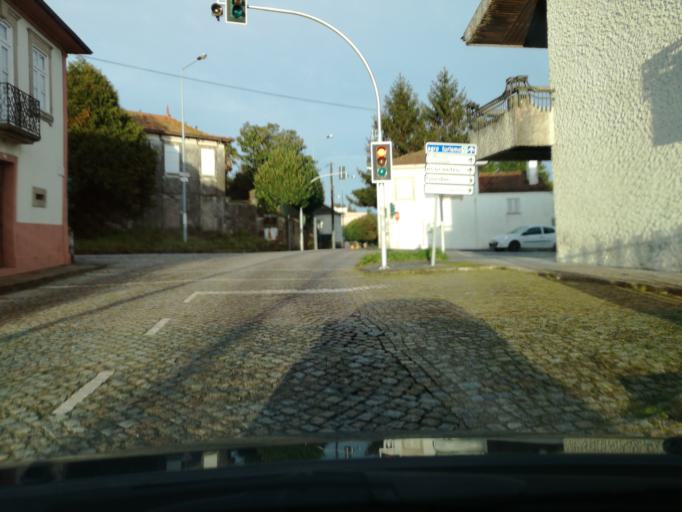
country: PT
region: Porto
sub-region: Maia
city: Anta
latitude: 41.2673
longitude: -8.6067
